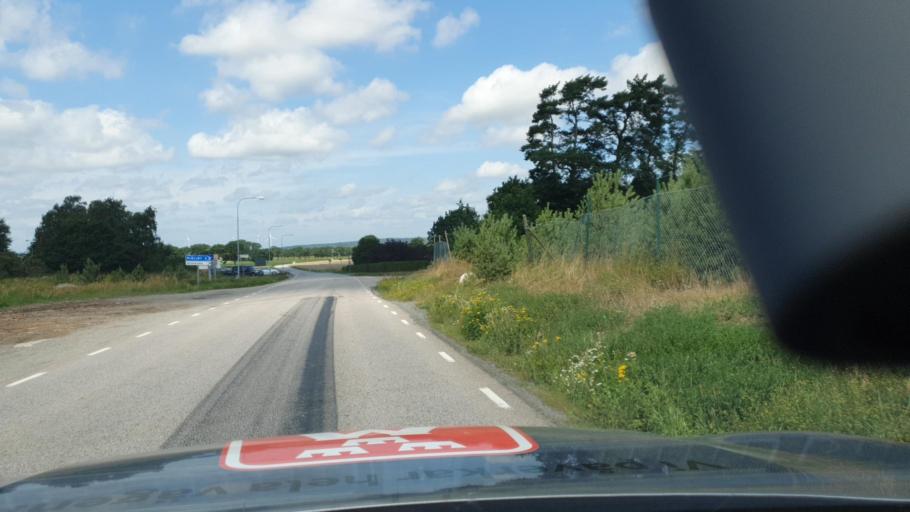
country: SE
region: Blekinge
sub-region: Solvesborgs Kommun
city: Soelvesborg
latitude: 56.0313
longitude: 14.6887
